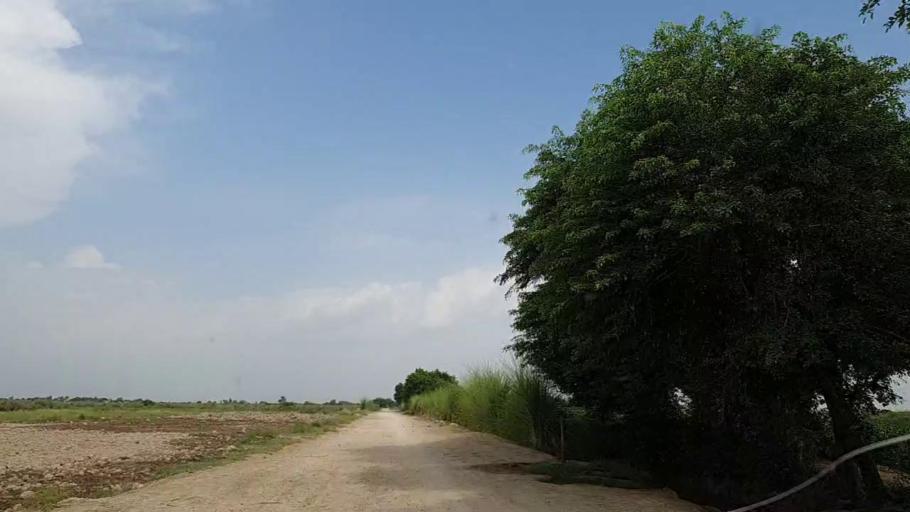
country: PK
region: Sindh
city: Khanpur
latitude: 27.8235
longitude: 69.5217
